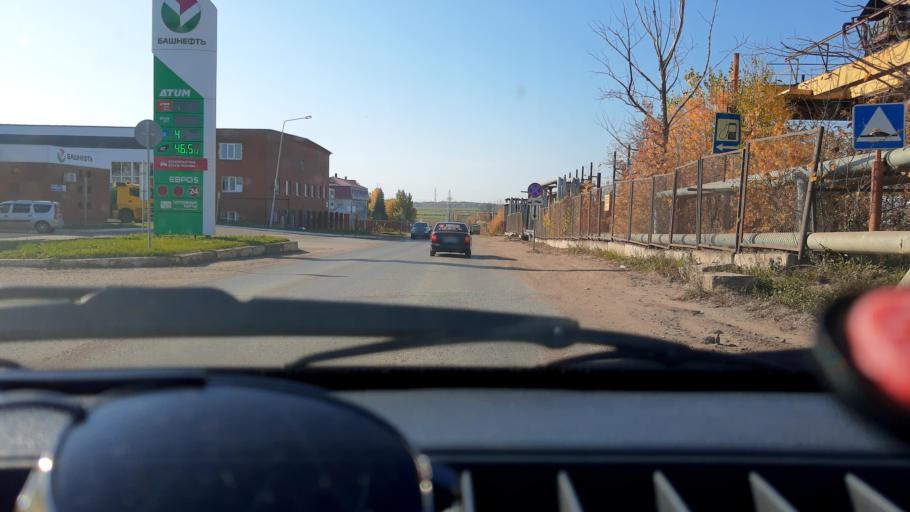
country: RU
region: Bashkortostan
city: Mikhaylovka
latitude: 54.8369
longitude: 55.8254
